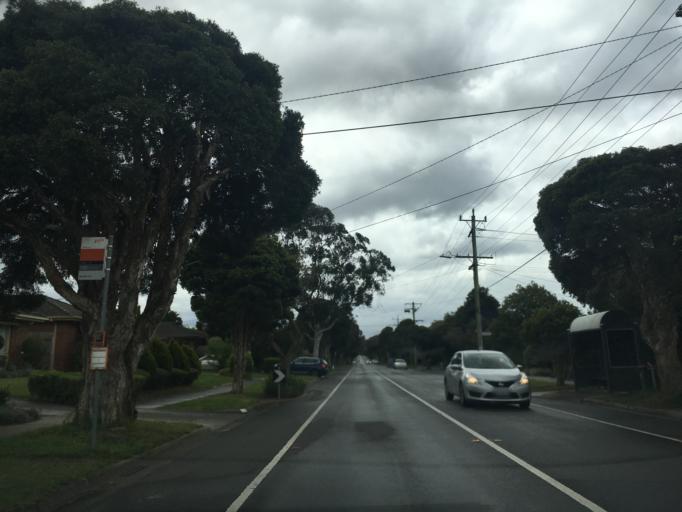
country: AU
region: Victoria
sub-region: Whitehorse
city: Vermont South
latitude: -37.8696
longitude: 145.1805
